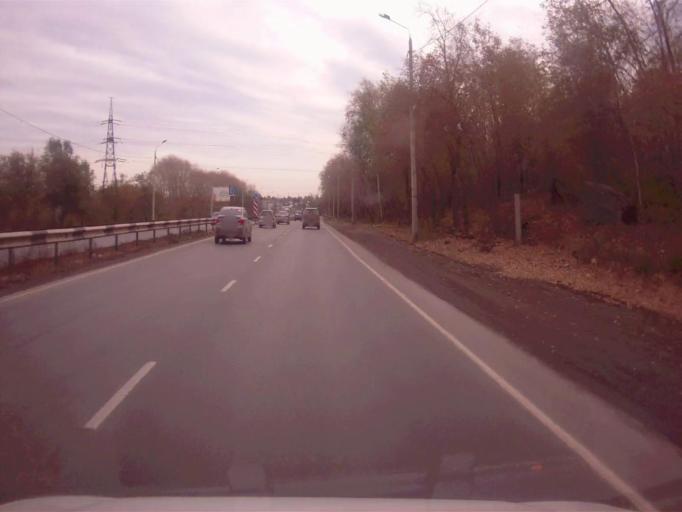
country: RU
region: Chelyabinsk
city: Novosineglazovskiy
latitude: 55.0511
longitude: 61.4123
